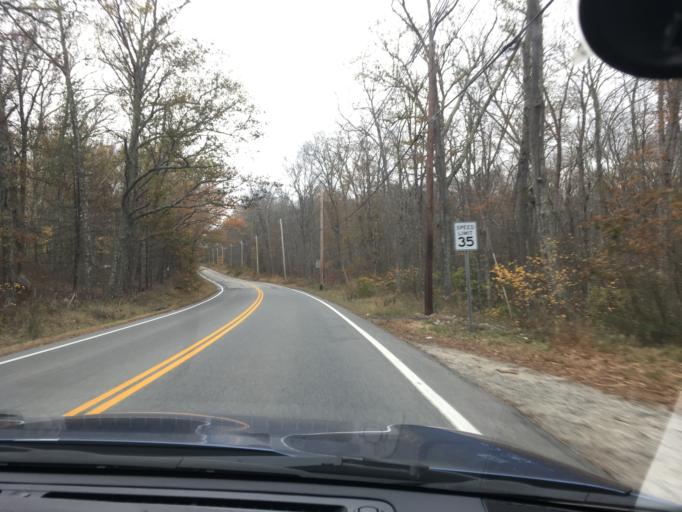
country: US
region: Rhode Island
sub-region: Providence County
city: North Scituate
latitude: 41.7963
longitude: -71.6583
